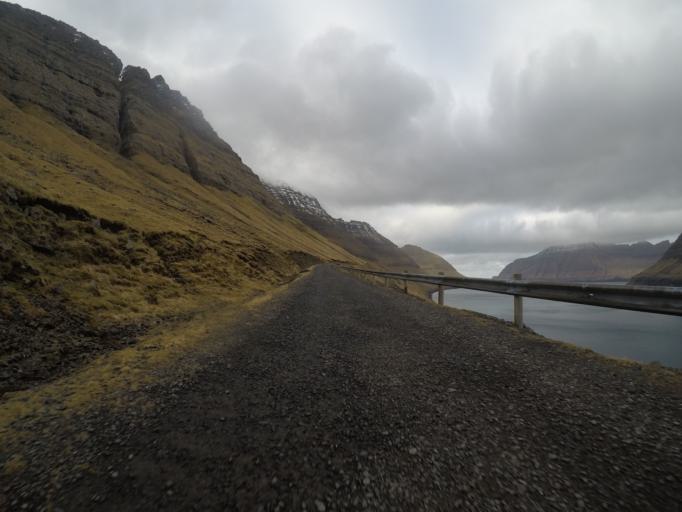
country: FO
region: Nordoyar
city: Klaksvik
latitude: 62.3247
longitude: -6.5636
